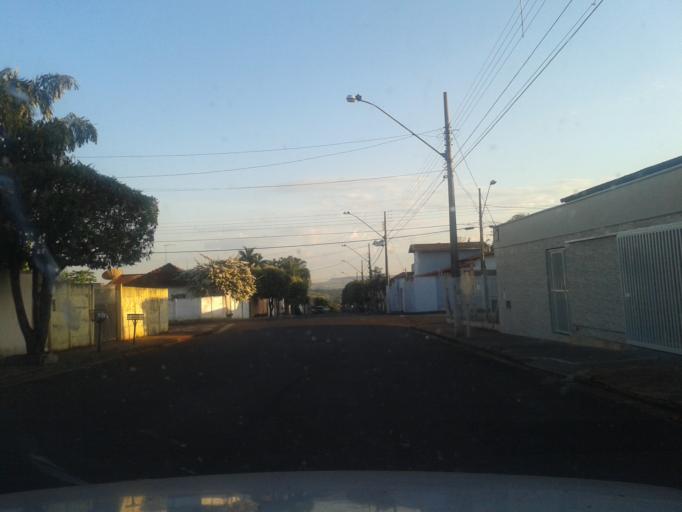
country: BR
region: Minas Gerais
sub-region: Ituiutaba
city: Ituiutaba
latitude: -18.9821
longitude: -49.4670
